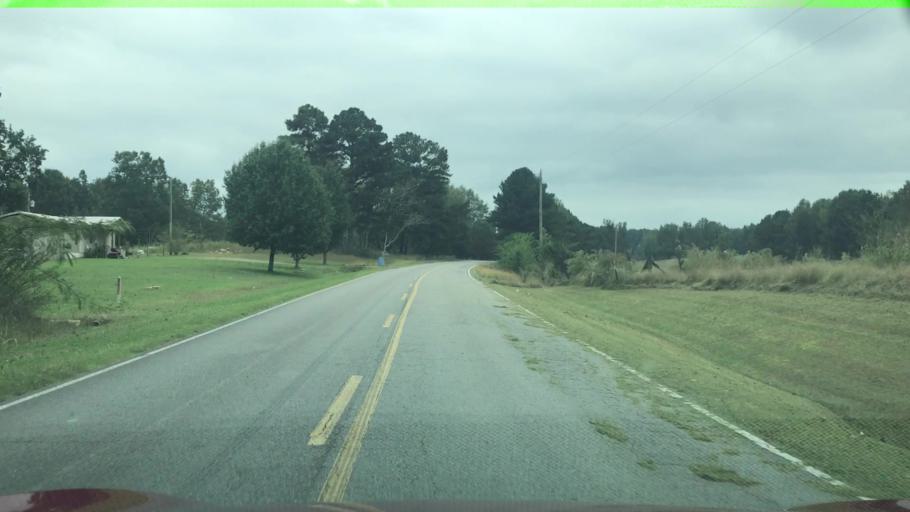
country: US
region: Alabama
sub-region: Cullman County
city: Good Hope
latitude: 34.1048
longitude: -87.0369
